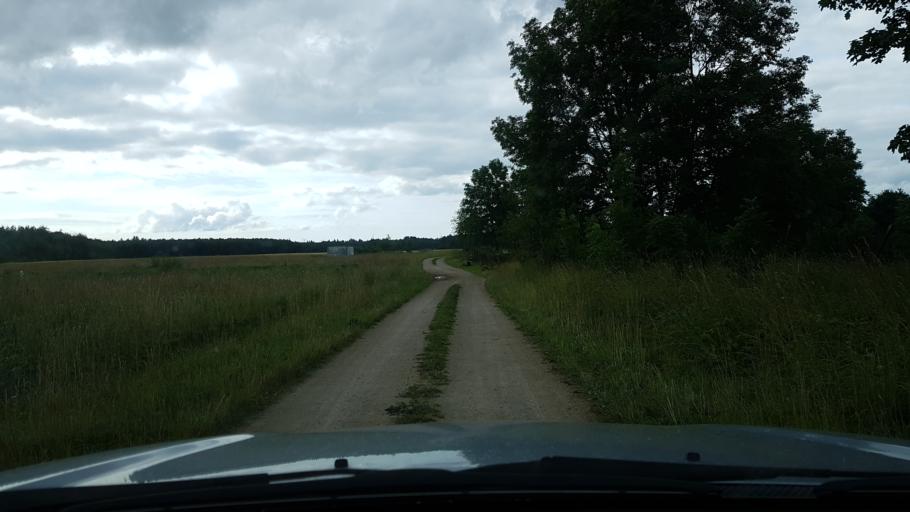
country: EE
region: Ida-Virumaa
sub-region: Narva-Joesuu linn
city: Narva-Joesuu
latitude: 59.3923
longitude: 28.0128
